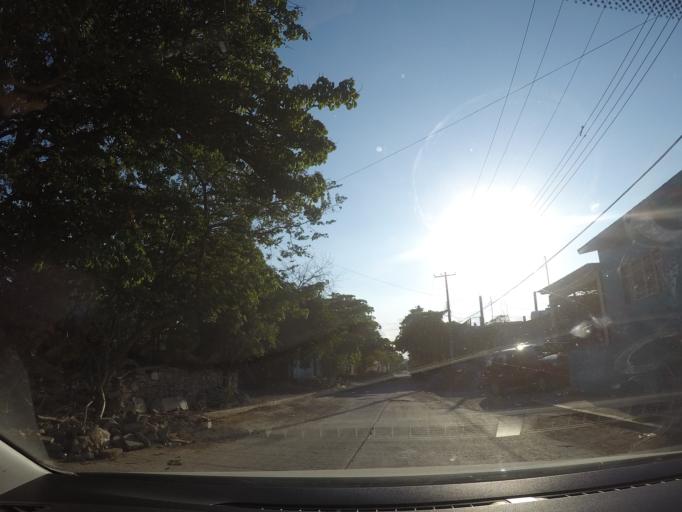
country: MX
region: Oaxaca
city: Juchitan de Zaragoza
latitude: 16.4347
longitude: -95.0281
